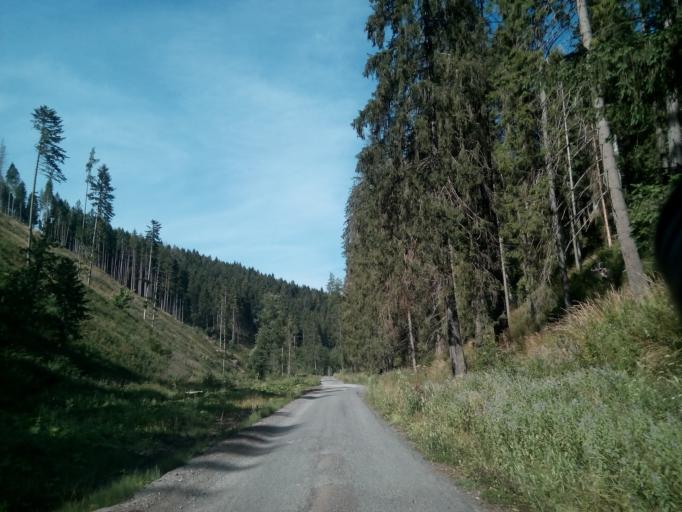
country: SK
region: Presovsky
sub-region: Okres Poprad
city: Svit
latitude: 48.9766
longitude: 20.2165
